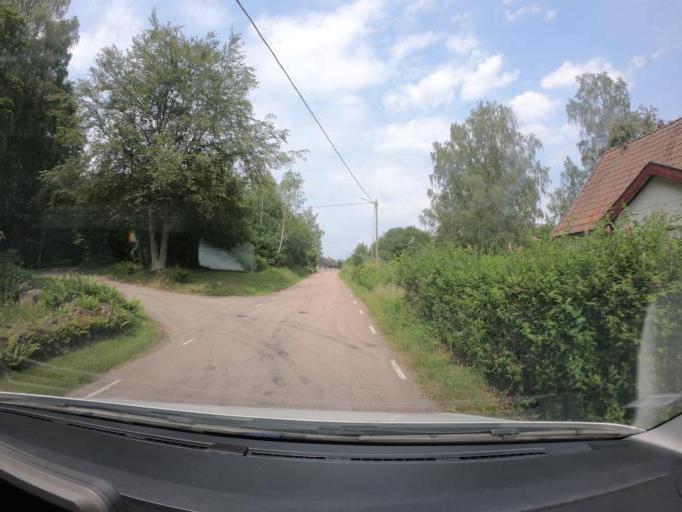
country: SE
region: Skane
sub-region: Hassleholms Kommun
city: Bjarnum
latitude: 56.2670
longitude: 13.7067
